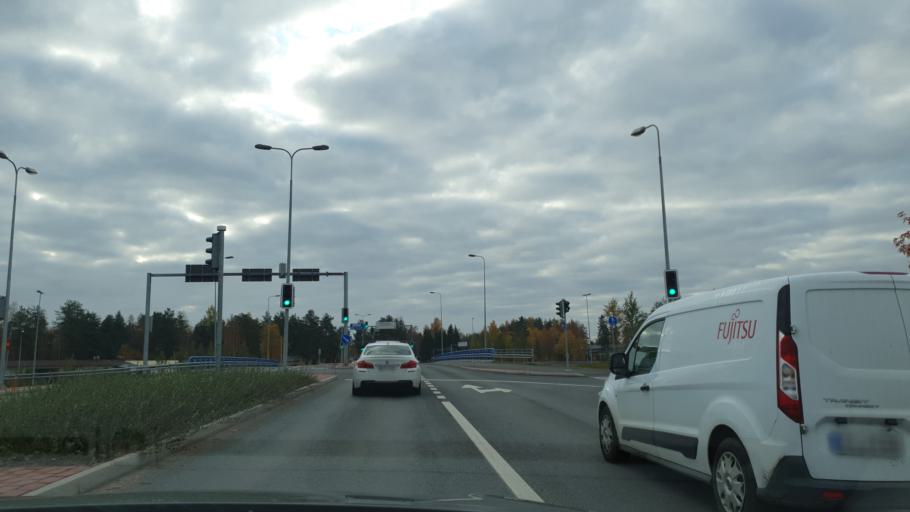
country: FI
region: Lapland
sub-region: Rovaniemi
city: Rovaniemi
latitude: 66.4911
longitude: 25.6923
